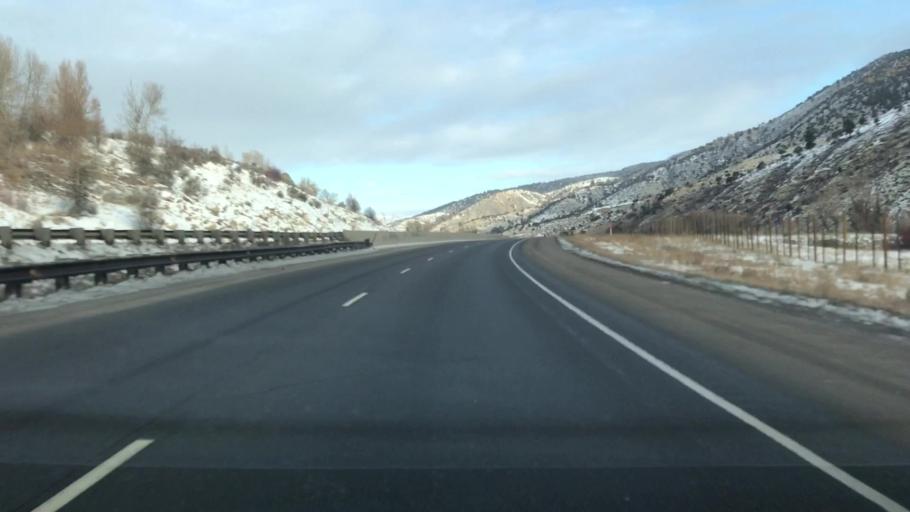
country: US
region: Colorado
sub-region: Eagle County
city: Edwards
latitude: 39.6761
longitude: -106.6477
